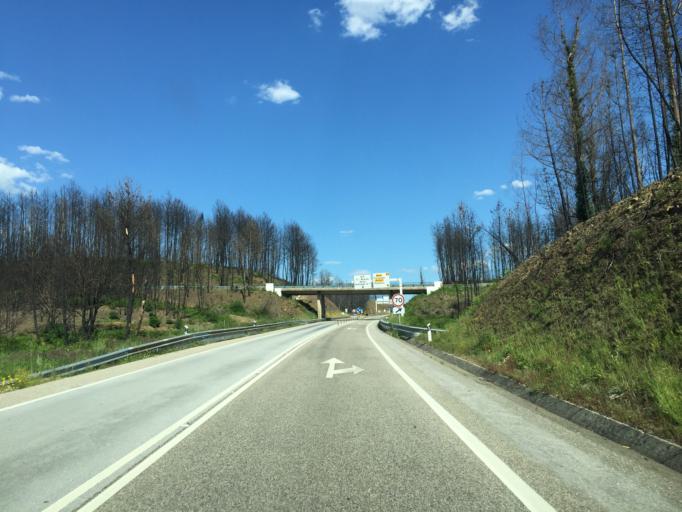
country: PT
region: Leiria
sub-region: Pedrogao Grande
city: Pedrogao Grande
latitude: 39.9278
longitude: -8.1832
